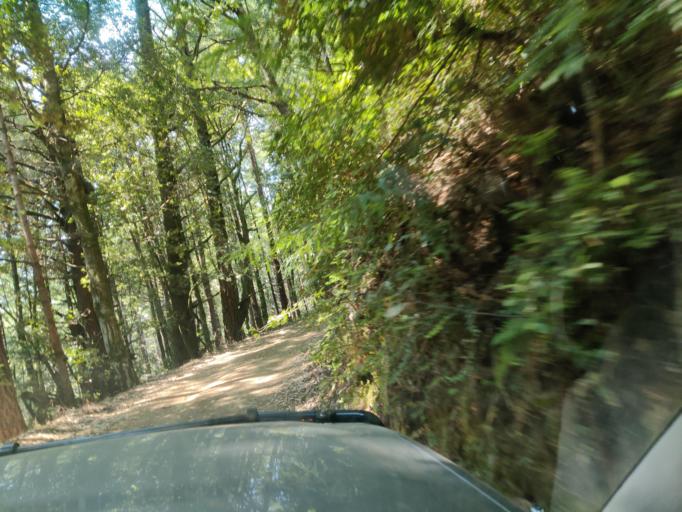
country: US
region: California
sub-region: Humboldt County
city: Redway
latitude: 39.9601
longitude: -123.9586
